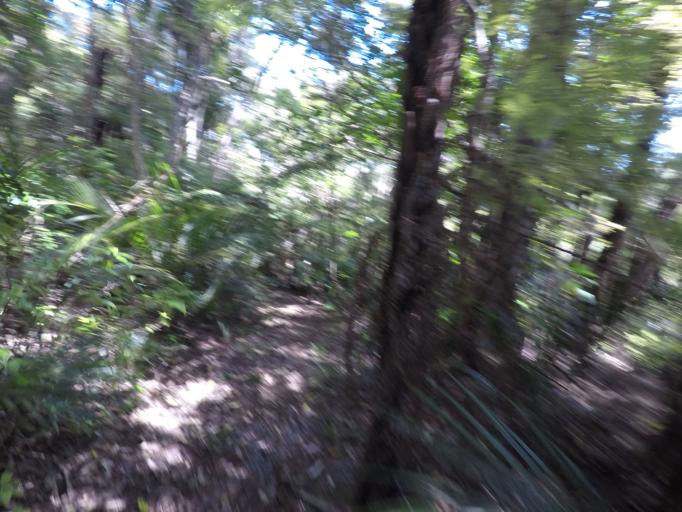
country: NZ
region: Auckland
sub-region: Auckland
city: Titirangi
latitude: -36.9708
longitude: 174.6325
